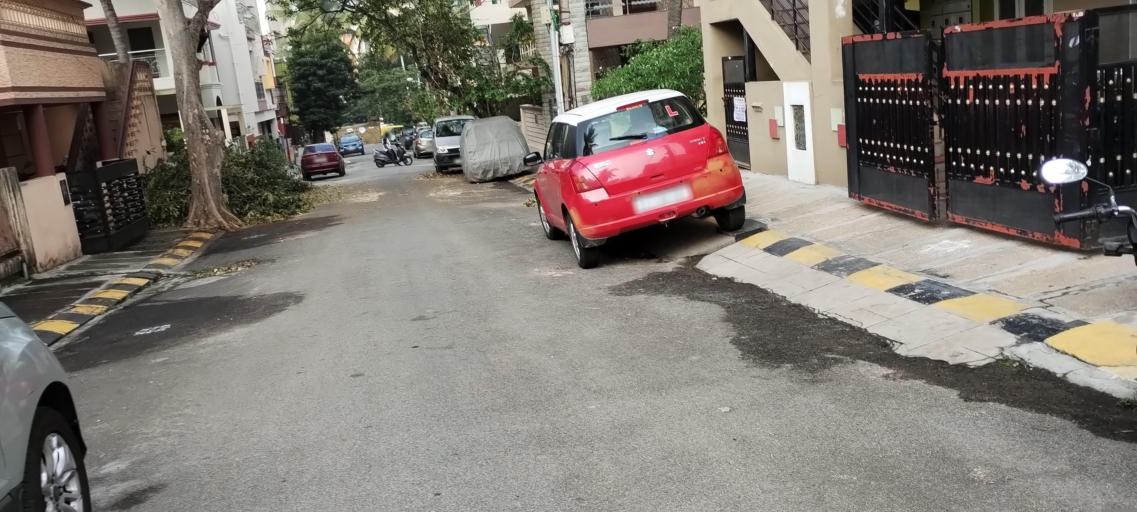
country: IN
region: Karnataka
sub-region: Bangalore Urban
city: Bangalore
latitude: 12.9404
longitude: 77.5435
